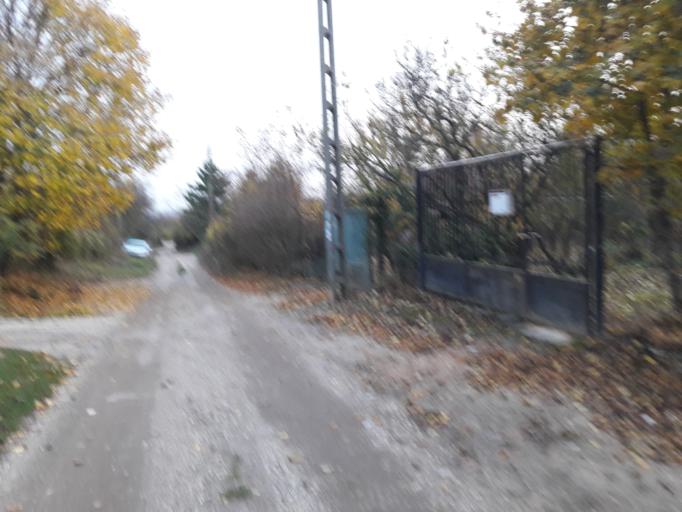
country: HU
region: Pest
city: Budaors
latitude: 47.4714
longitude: 18.9793
